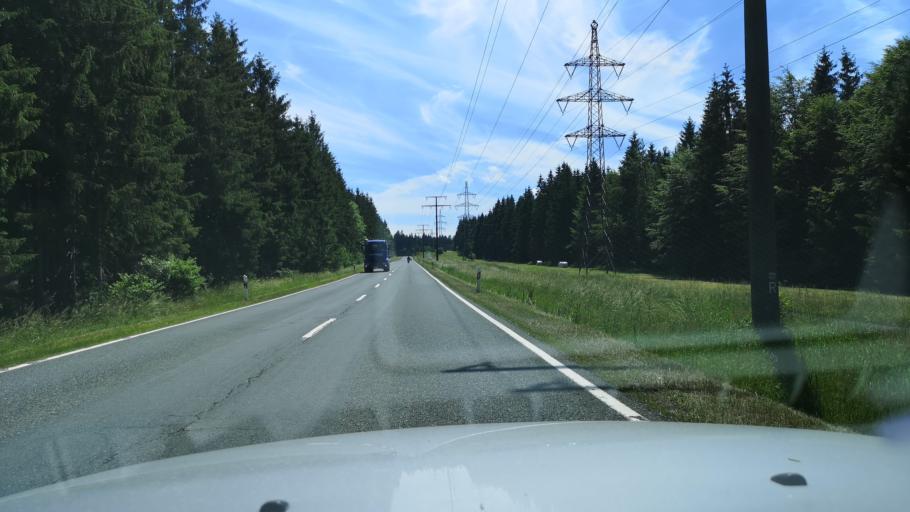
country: DE
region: Bavaria
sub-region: Upper Franconia
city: Tettau
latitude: 50.4737
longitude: 11.3092
